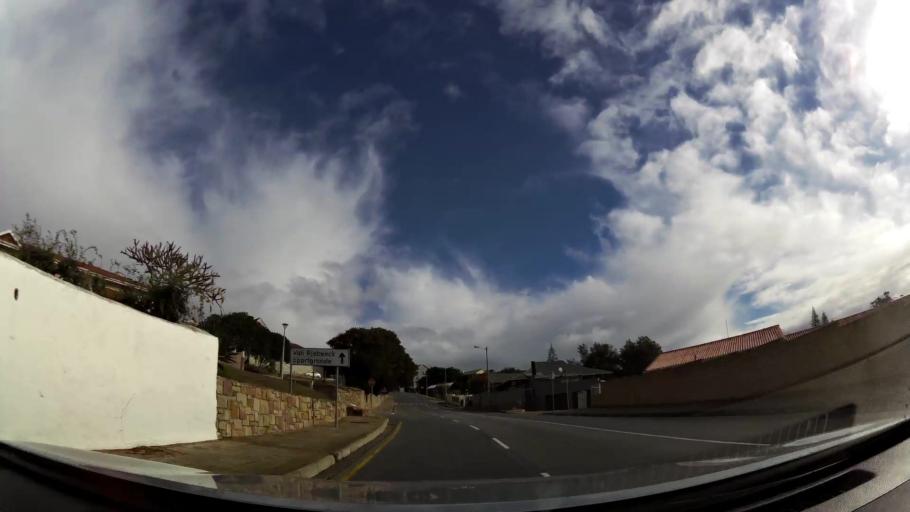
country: ZA
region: Western Cape
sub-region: Eden District Municipality
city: Mossel Bay
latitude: -34.1846
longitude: 22.1417
